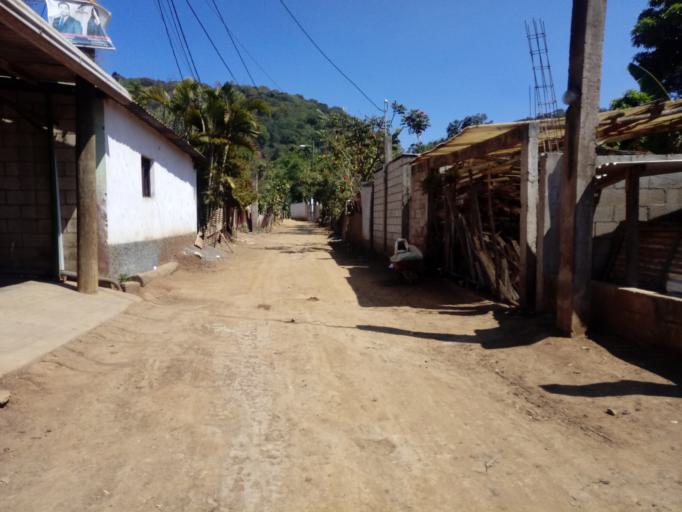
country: GT
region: Escuintla
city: San Vicente Pacaya
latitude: 14.4412
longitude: -90.6186
